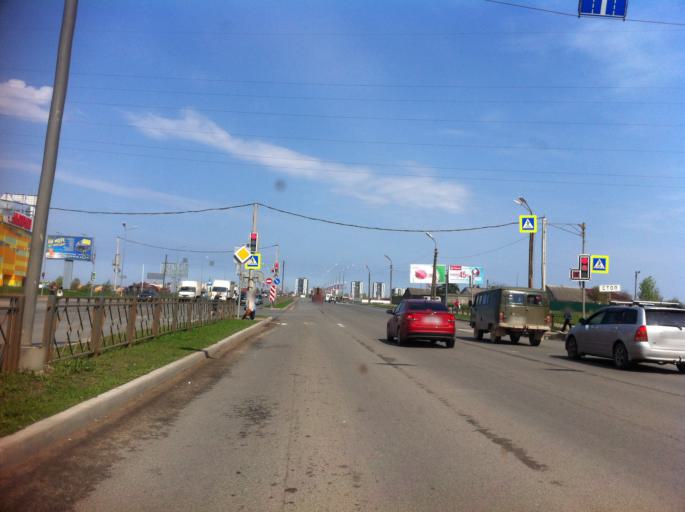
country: RU
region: Pskov
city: Pskov
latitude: 57.8223
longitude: 28.2929
